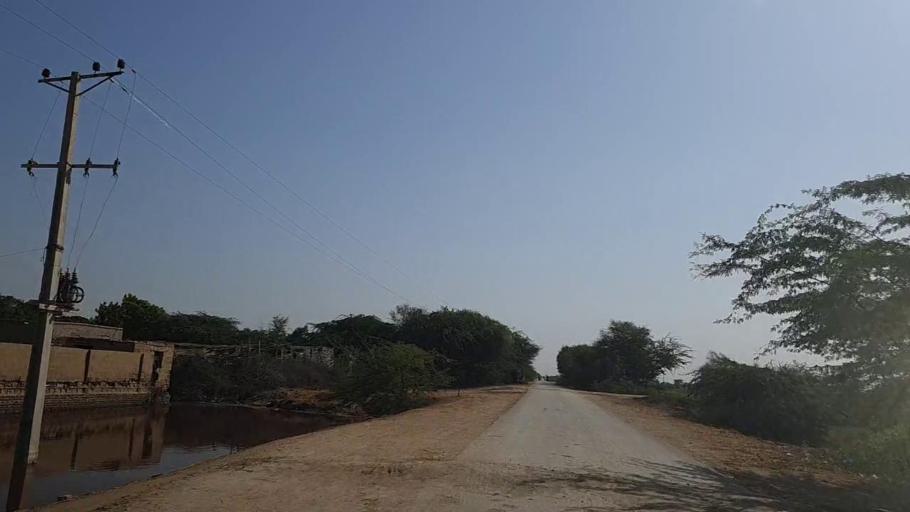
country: PK
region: Sindh
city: Mirpur Batoro
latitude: 24.6394
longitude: 68.2911
